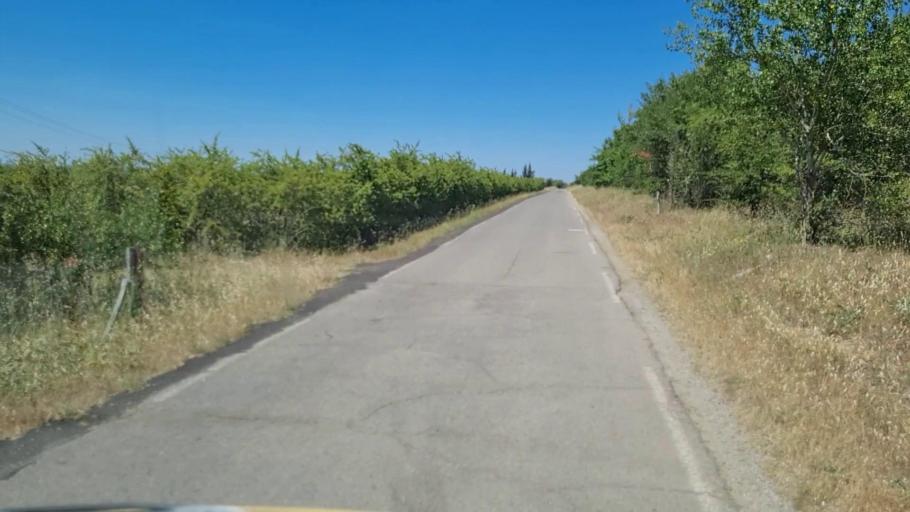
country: FR
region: Languedoc-Roussillon
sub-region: Departement du Gard
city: Vauvert
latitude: 43.6725
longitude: 4.2641
